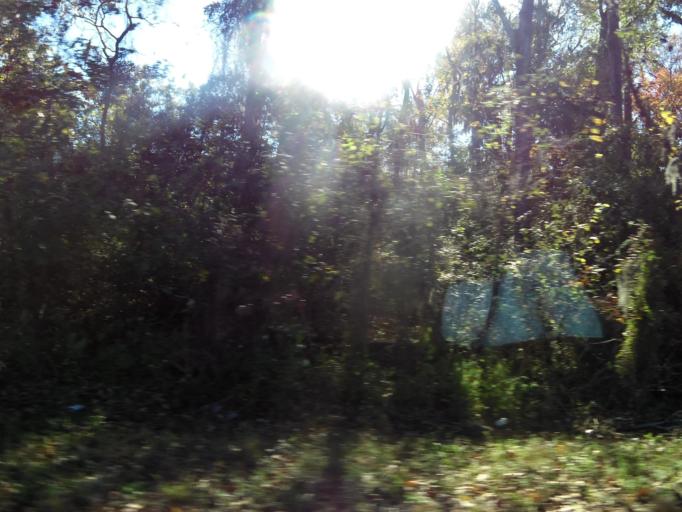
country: US
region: Georgia
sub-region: Chatham County
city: Savannah
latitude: 32.0651
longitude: -81.1457
